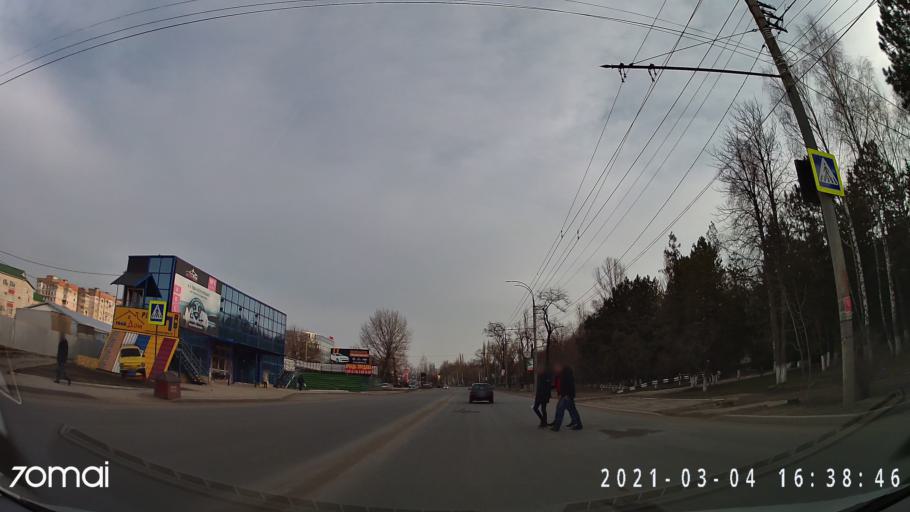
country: MD
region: Balti
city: Balti
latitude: 47.7790
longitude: 27.8926
